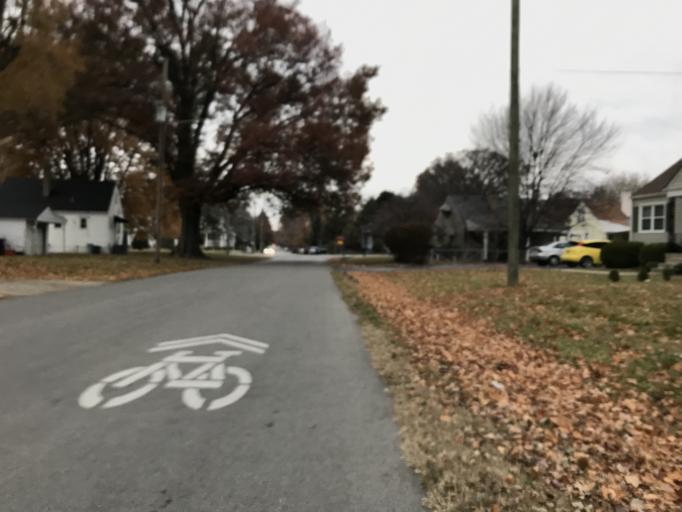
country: US
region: Kentucky
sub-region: Jefferson County
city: Audubon Park
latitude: 38.2148
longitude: -85.7366
